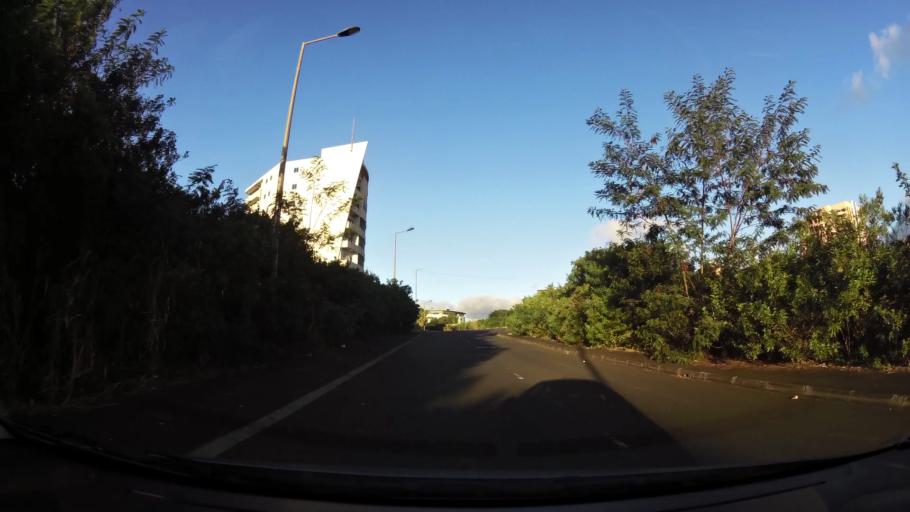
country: MU
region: Plaines Wilhems
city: Ebene
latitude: -20.2408
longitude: 57.4913
